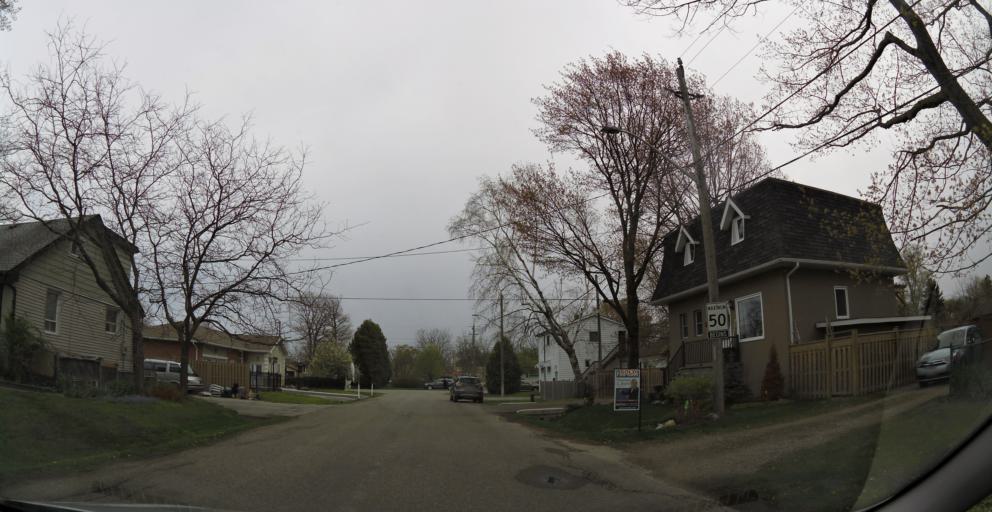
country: CA
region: Ontario
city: Mississauga
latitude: 43.5628
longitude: -79.5818
